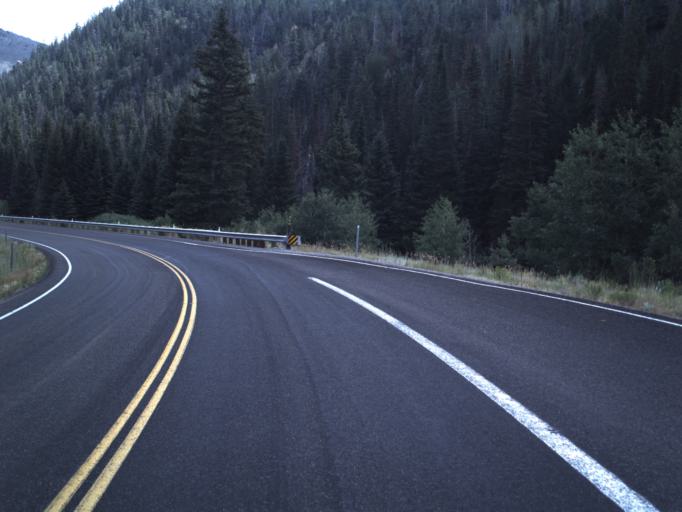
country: US
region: Utah
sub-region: Summit County
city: Francis
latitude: 40.4713
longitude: -110.9193
